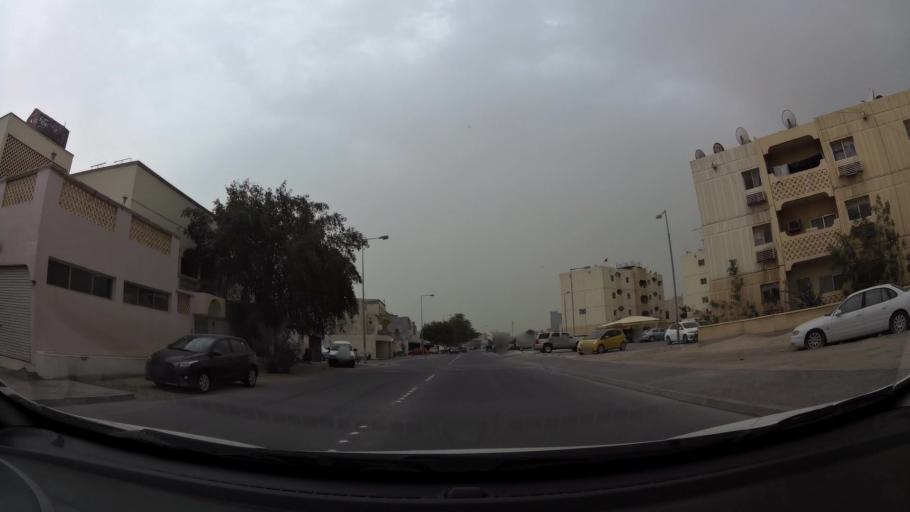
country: BH
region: Northern
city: Madinat `Isa
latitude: 26.1739
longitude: 50.5427
